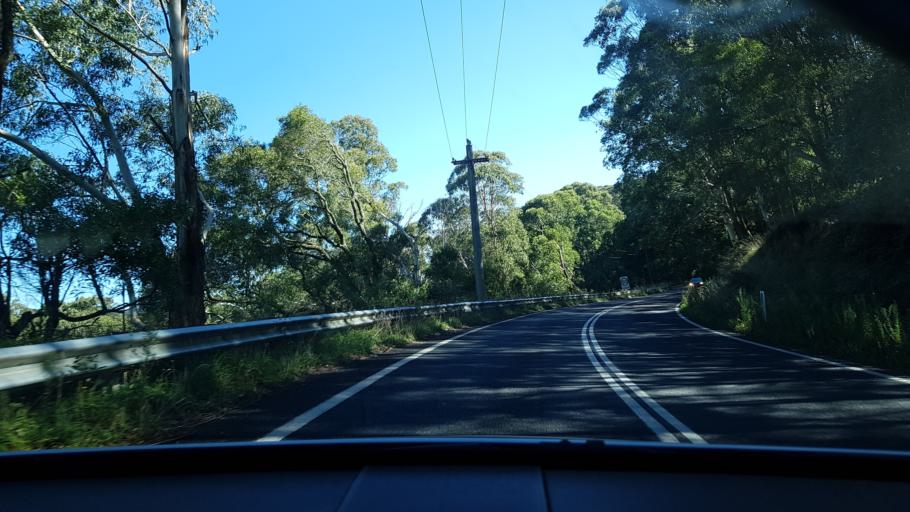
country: AU
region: New South Wales
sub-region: Lithgow
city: Bowenfels
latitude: -33.6403
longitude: 150.0528
